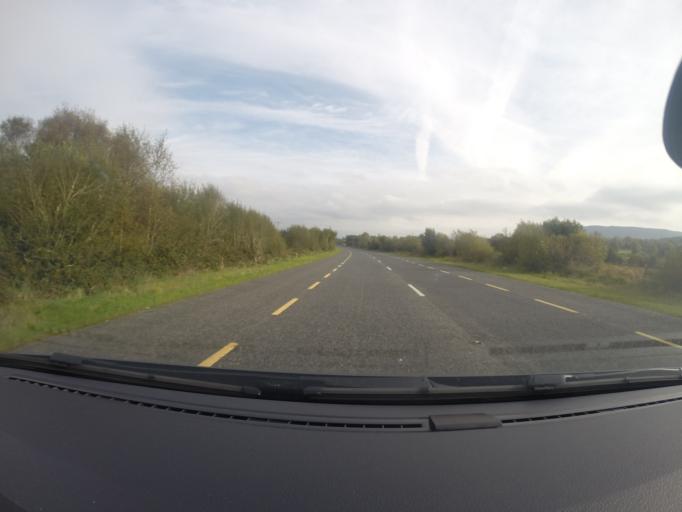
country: IE
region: Connaught
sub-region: County Leitrim
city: Manorhamilton
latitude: 54.3141
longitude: -8.2637
